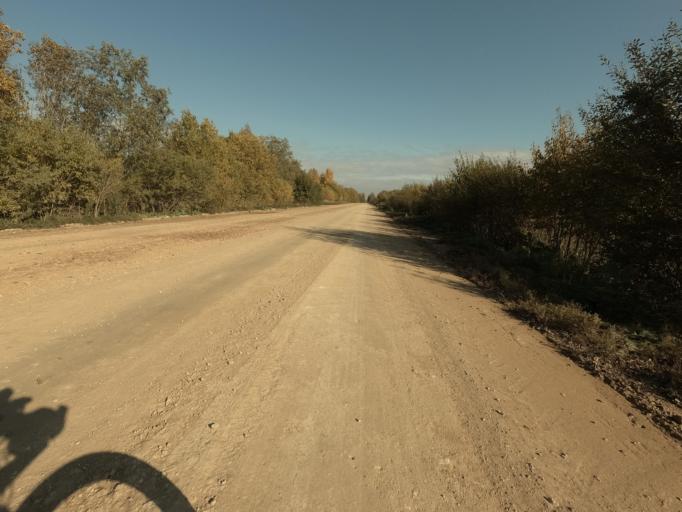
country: RU
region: Novgorod
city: Batetskiy
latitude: 58.8218
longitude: 30.7044
